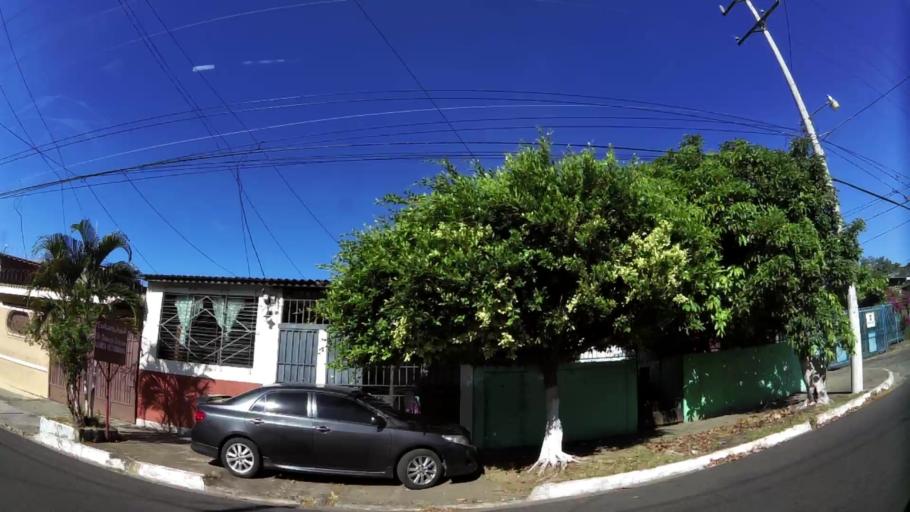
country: SV
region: Sonsonate
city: Sonzacate
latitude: 13.7298
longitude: -89.7171
